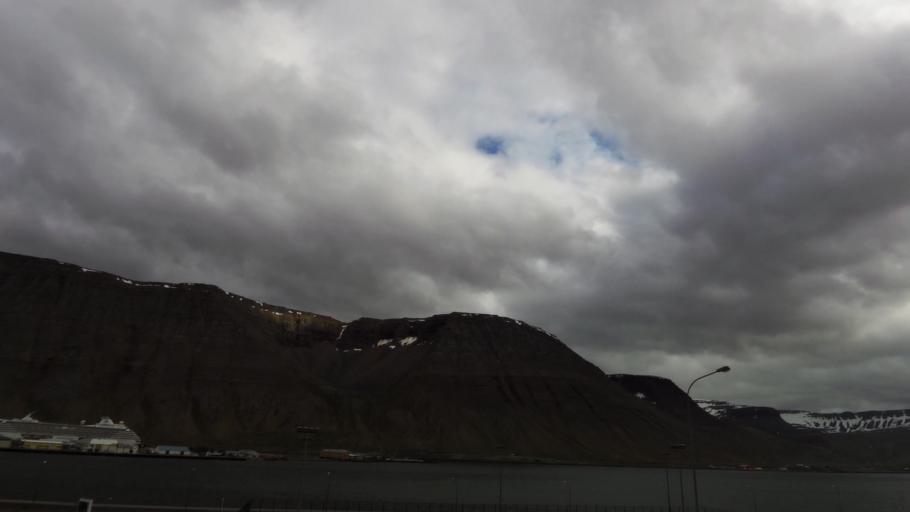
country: IS
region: Westfjords
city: Isafjoerdur
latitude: 66.0726
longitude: -23.1388
